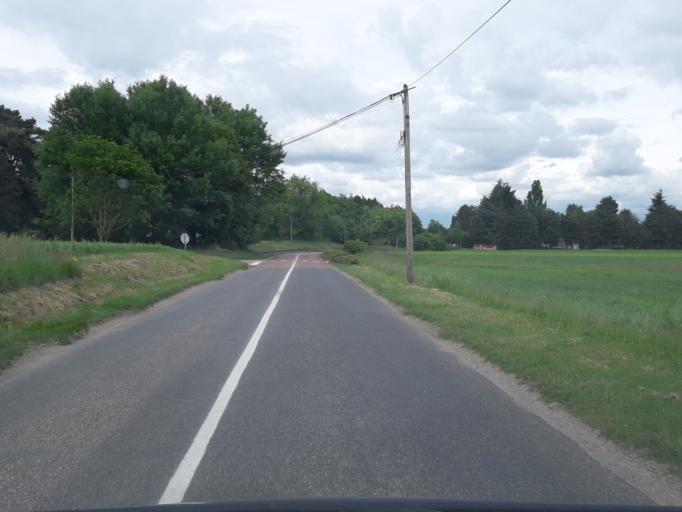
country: FR
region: Ile-de-France
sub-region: Departement de l'Essonne
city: Boissy-le-Cutte
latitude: 48.4357
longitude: 2.2878
